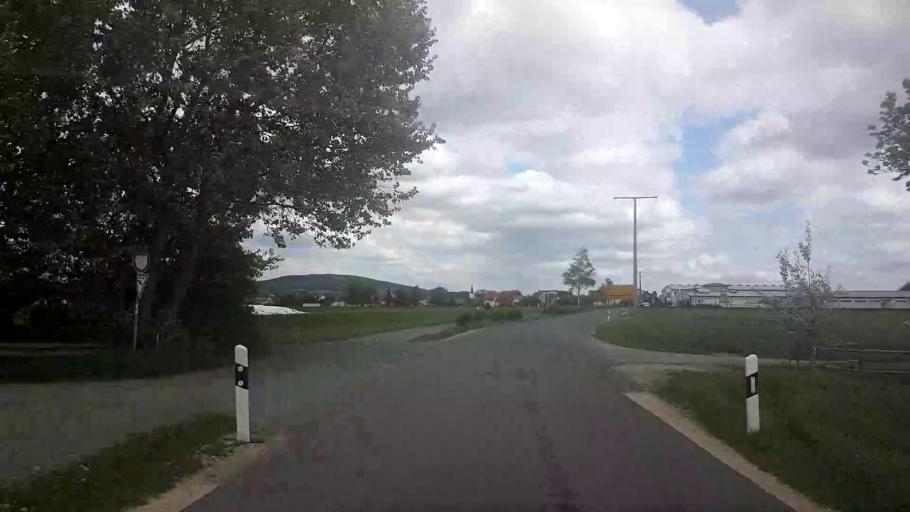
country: DE
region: Bavaria
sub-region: Upper Franconia
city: Bad Staffelstein
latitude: 50.1272
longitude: 11.0208
